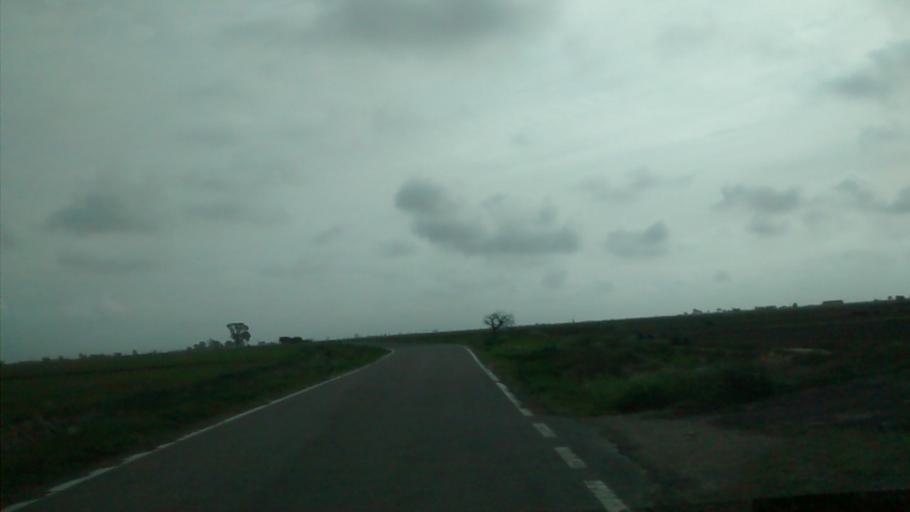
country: ES
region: Catalonia
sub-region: Provincia de Tarragona
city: Sant Carles de la Rapita
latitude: 40.6436
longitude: 0.6063
